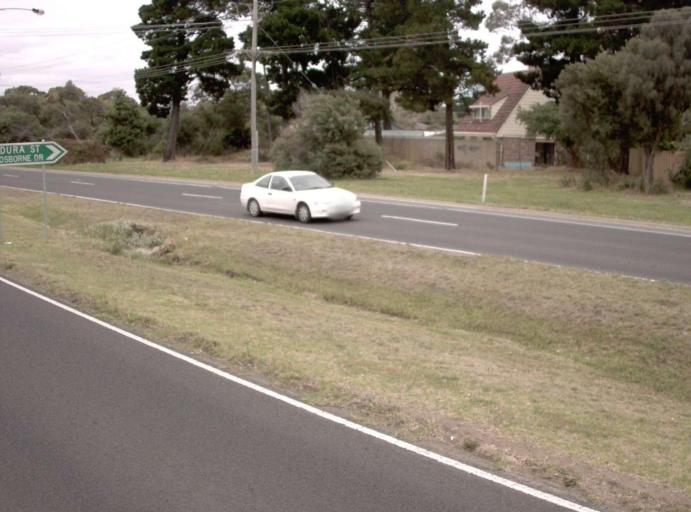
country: AU
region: Victoria
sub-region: Mornington Peninsula
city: Mount Martha
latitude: -38.2473
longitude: 145.0373
